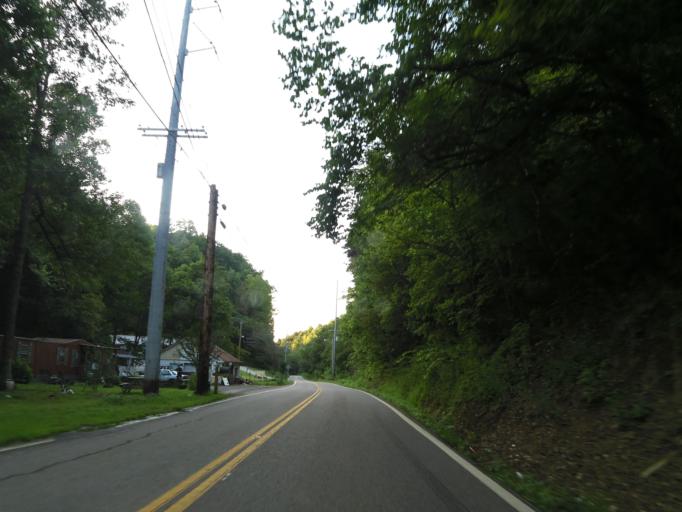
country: US
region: Tennessee
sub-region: Union County
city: Luttrell
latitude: 36.1881
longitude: -83.7417
